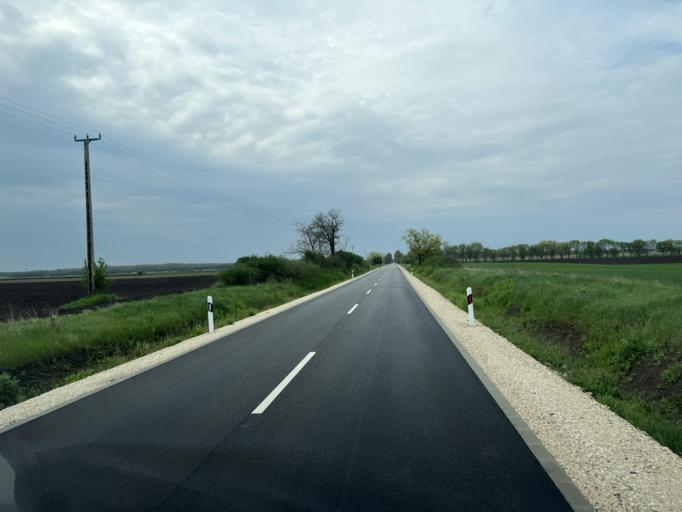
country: HU
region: Pest
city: Nyaregyhaza
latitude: 47.2438
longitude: 19.5206
